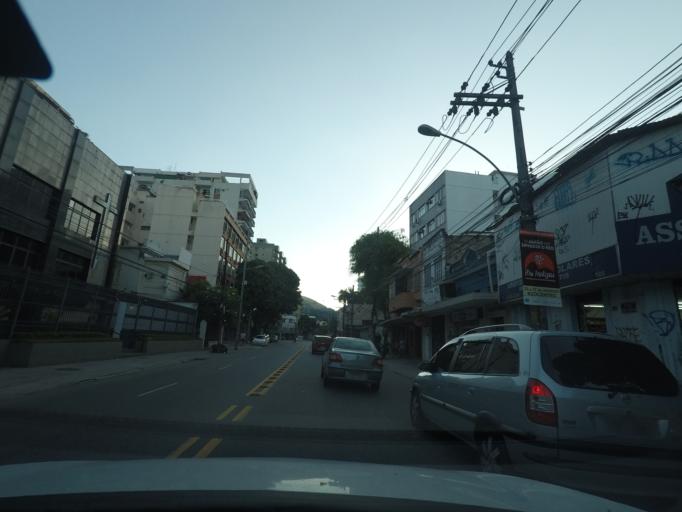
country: BR
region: Rio de Janeiro
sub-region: Rio De Janeiro
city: Rio de Janeiro
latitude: -22.9345
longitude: -43.2429
